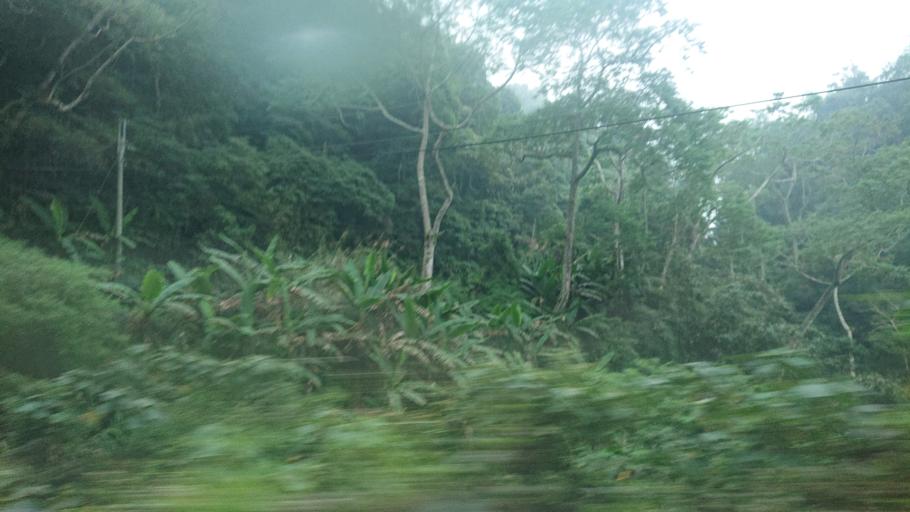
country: TW
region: Taiwan
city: Lugu
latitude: 23.5984
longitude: 120.7144
